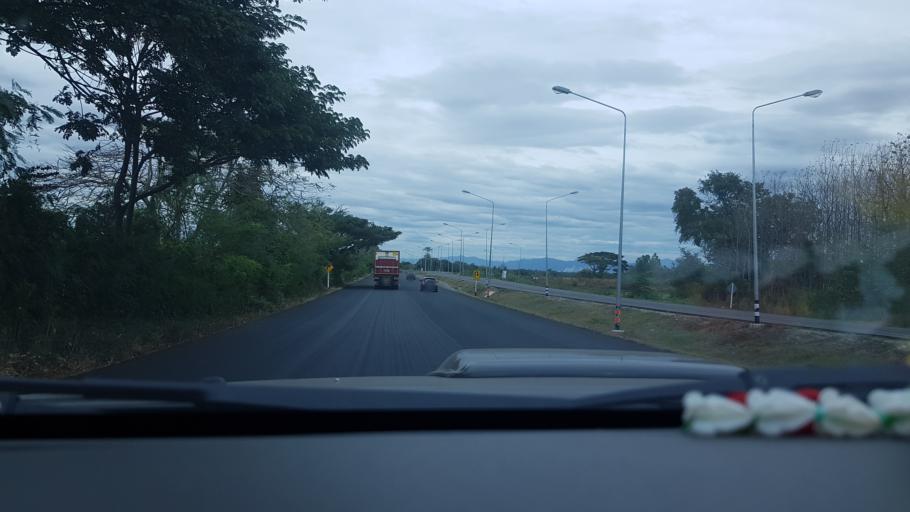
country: TH
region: Phetchabun
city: Phetchabun
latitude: 16.4890
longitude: 101.1405
